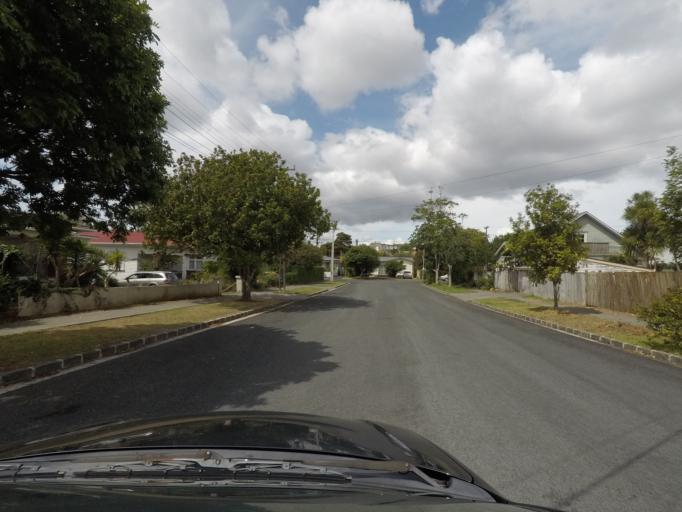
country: NZ
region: Auckland
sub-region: Auckland
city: Rosebank
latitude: -36.8831
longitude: 174.7086
